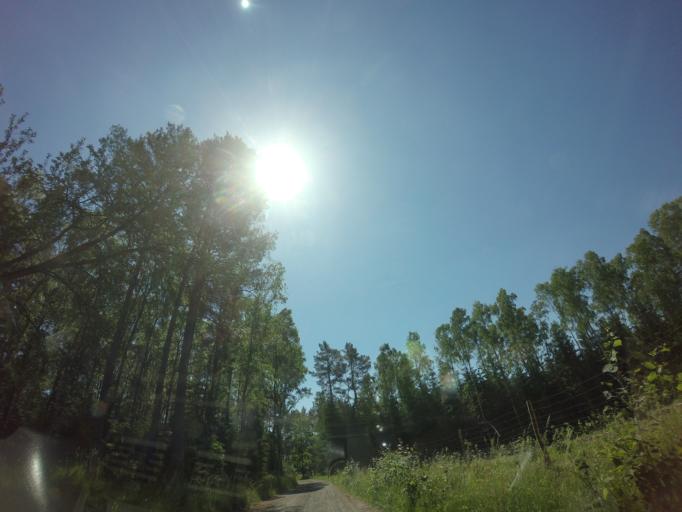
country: PL
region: West Pomeranian Voivodeship
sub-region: Powiat walecki
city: Miroslawiec
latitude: 53.2399
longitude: 16.0393
